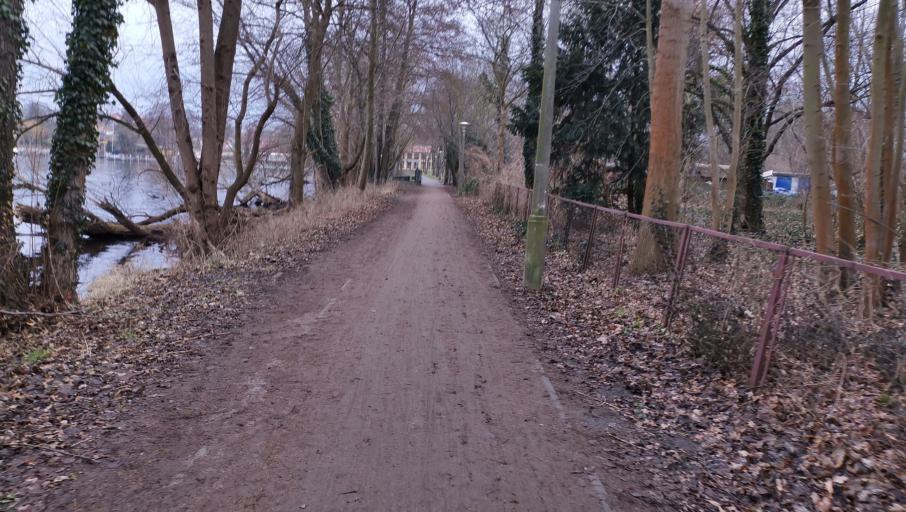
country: DE
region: Brandenburg
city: Potsdam
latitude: 52.3872
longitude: 13.0384
